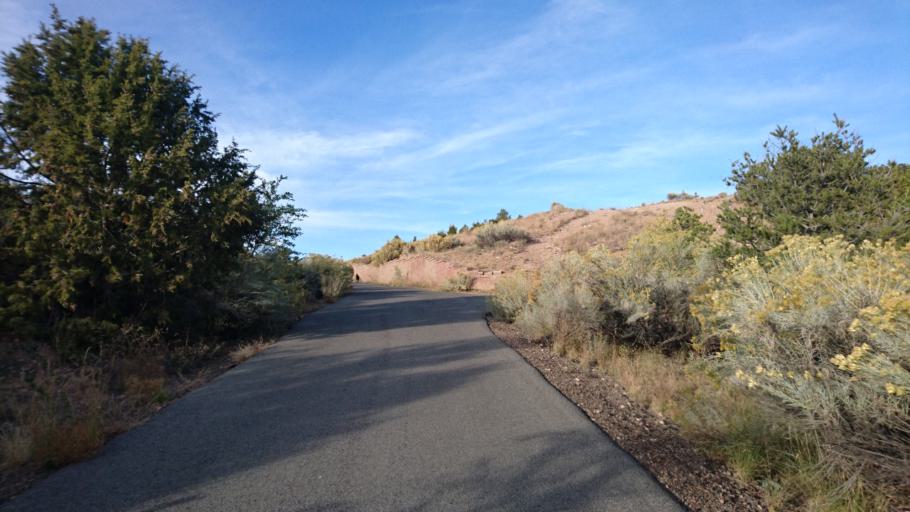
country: US
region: New Mexico
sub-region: Santa Fe County
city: Santa Fe
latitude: 35.6494
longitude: -105.9654
